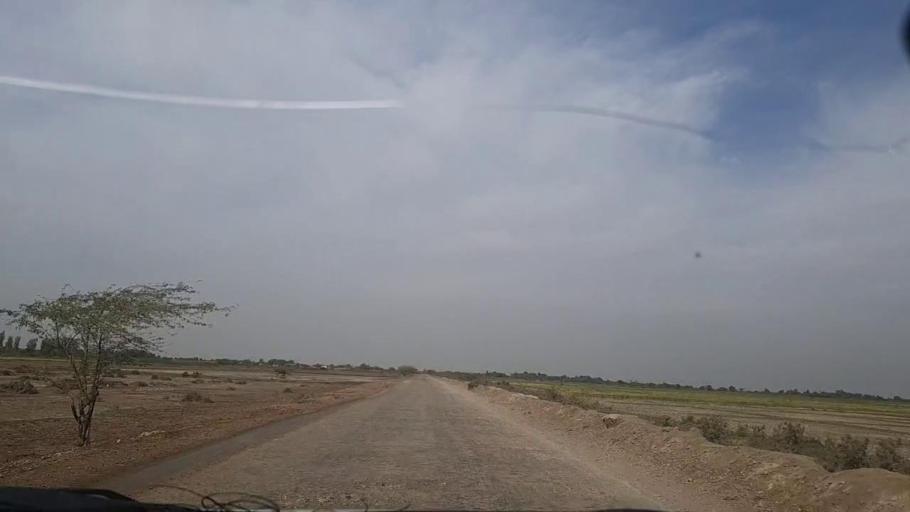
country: PK
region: Sindh
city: Pithoro
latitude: 25.5348
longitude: 69.3606
